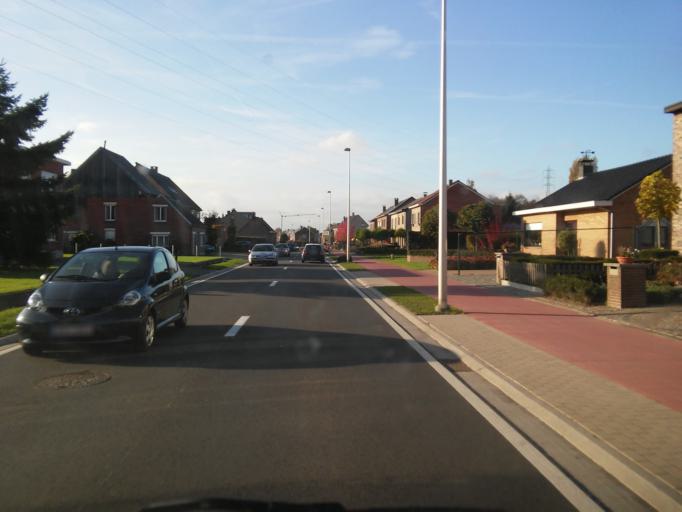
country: BE
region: Flanders
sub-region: Provincie Antwerpen
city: Duffel
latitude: 51.0919
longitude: 4.5303
